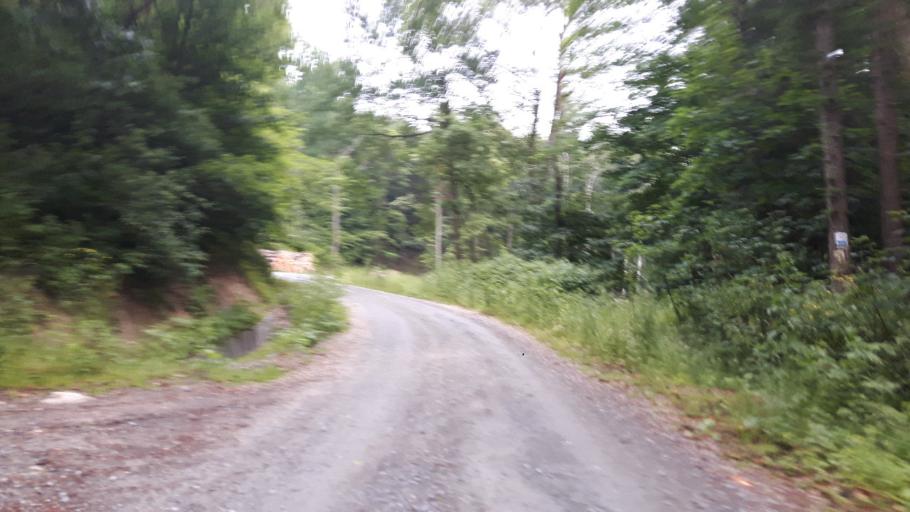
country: PL
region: Warmian-Masurian Voivodeship
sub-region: Powiat elblaski
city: Tolkmicko
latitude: 54.3353
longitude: 19.5674
